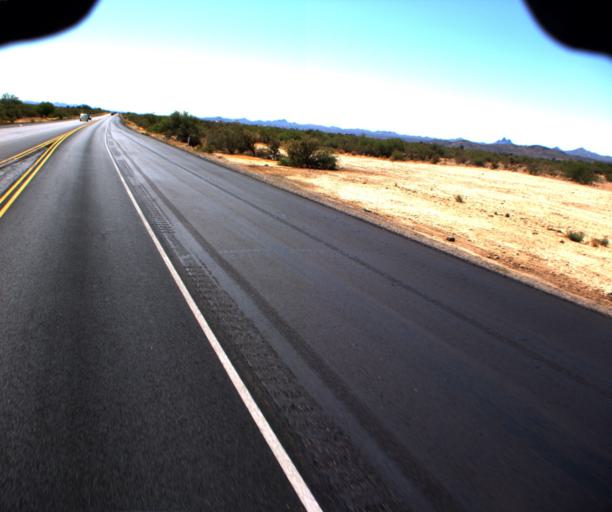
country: US
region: Arizona
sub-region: Yavapai County
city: Congress
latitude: 34.0552
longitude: -112.8527
